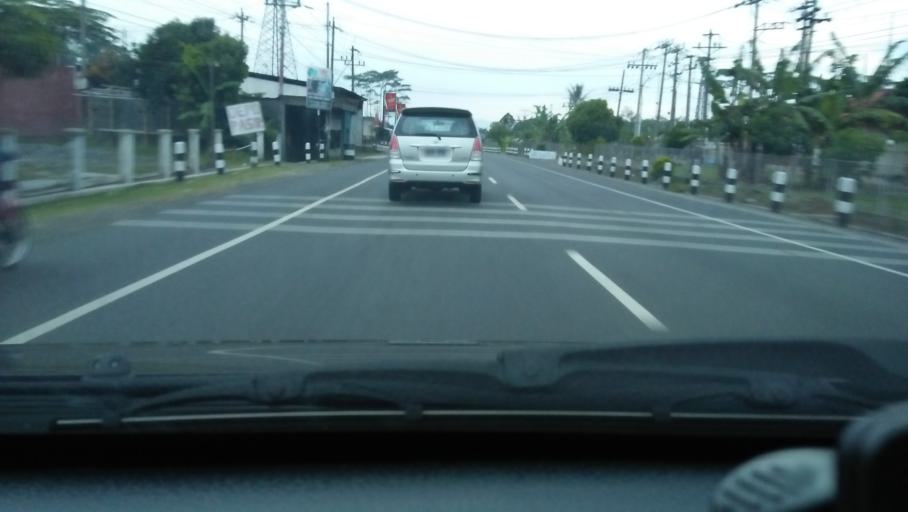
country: ID
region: Central Java
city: Magelang
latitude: -7.4160
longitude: 110.2347
